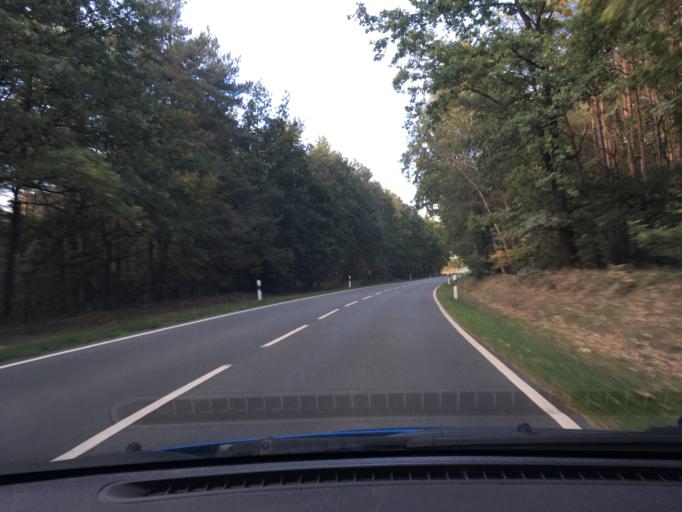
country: DE
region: Lower Saxony
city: Fassberg
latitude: 52.9201
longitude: 10.1270
